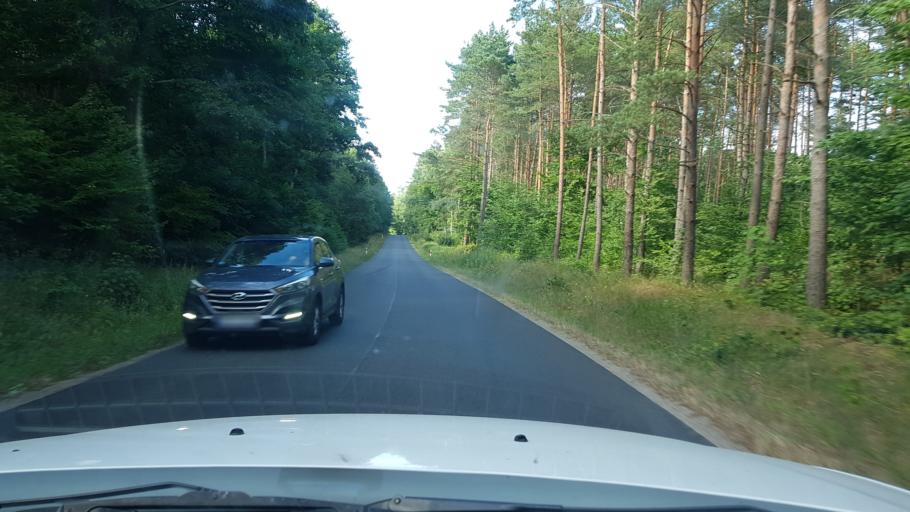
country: PL
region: West Pomeranian Voivodeship
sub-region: Powiat drawski
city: Zlocieniec
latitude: 53.5589
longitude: 16.0103
